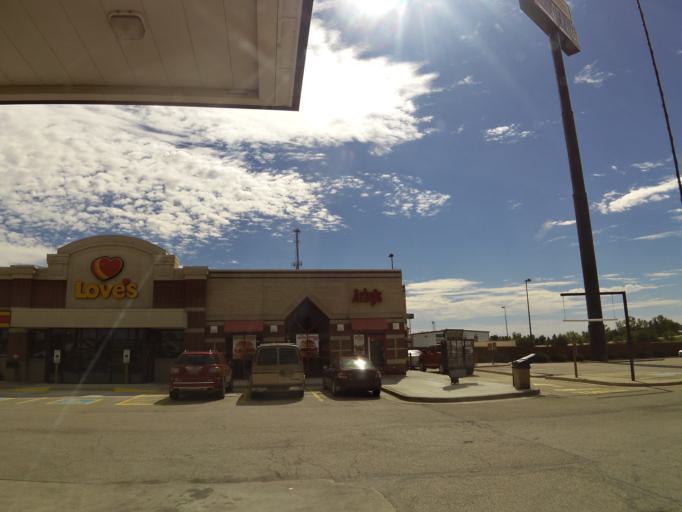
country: US
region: Illinois
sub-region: McLean County
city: Le Roy
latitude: 40.3407
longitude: -88.7613
